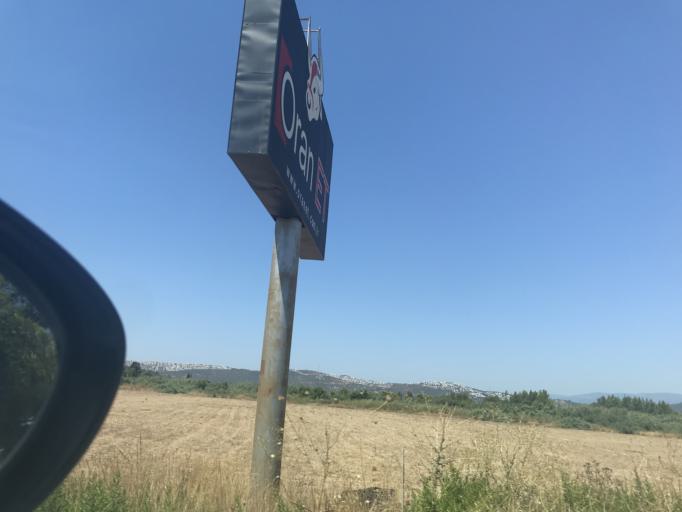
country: TR
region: Mugla
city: Kiulukioi
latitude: 37.1702
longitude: 27.5967
